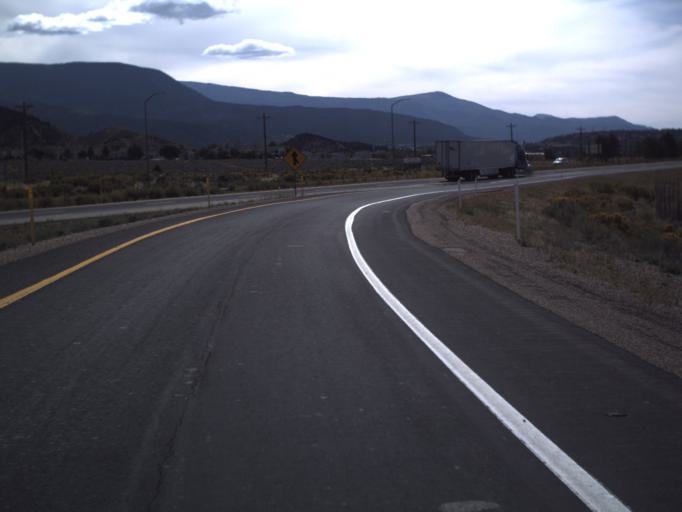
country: US
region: Utah
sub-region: Iron County
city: Cedar City
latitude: 37.7270
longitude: -113.0548
